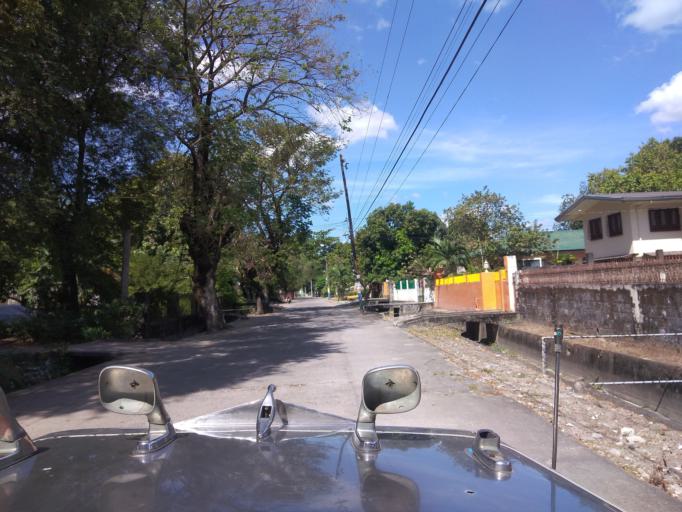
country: PH
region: Central Luzon
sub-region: Province of Pampanga
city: Santa Rita
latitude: 15.0039
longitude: 120.6014
